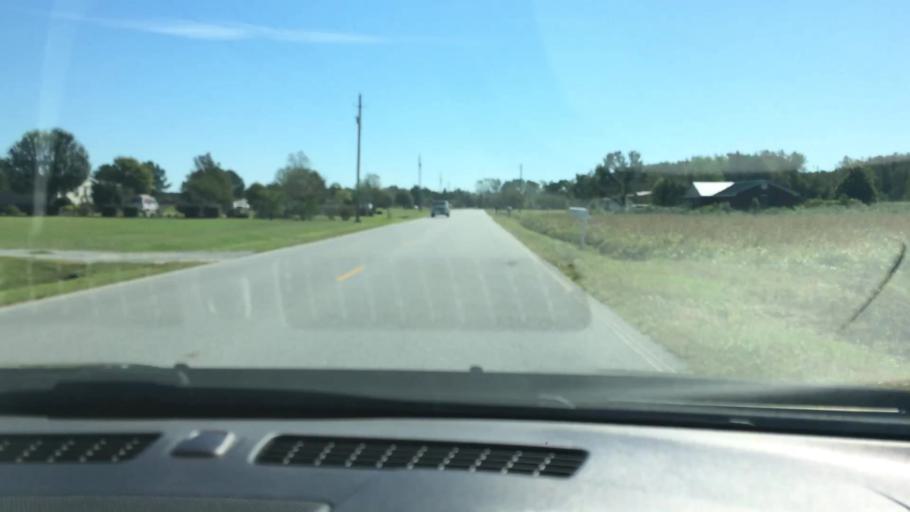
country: US
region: North Carolina
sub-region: Pitt County
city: Grifton
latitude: 35.3813
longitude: -77.3726
